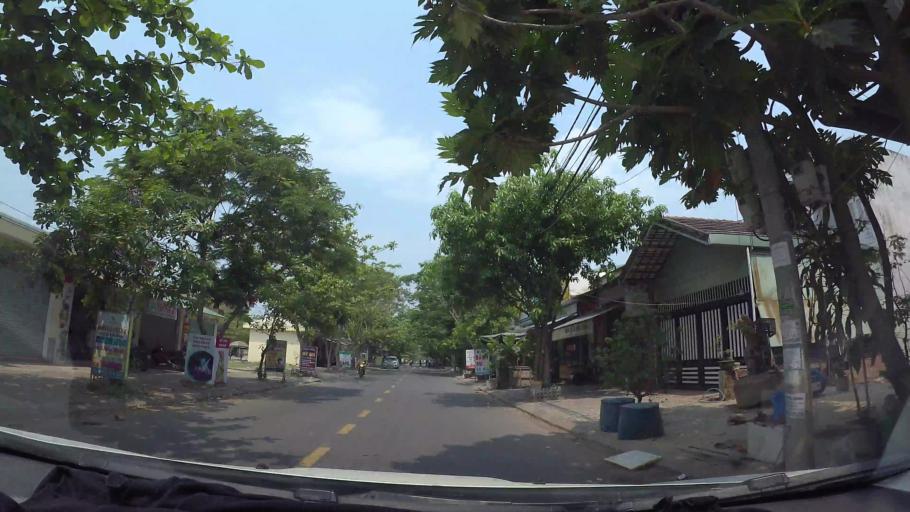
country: VN
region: Da Nang
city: Cam Le
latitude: 16.0064
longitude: 108.2153
